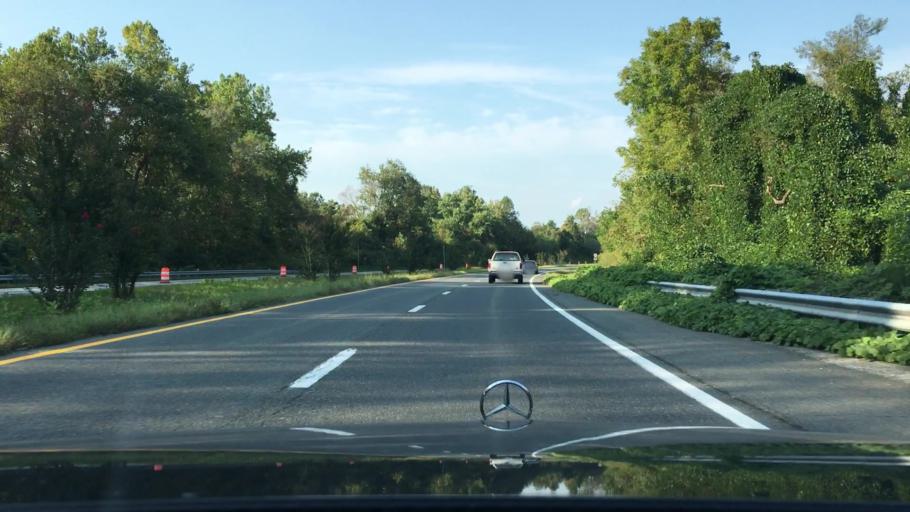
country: US
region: Virginia
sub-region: Amherst County
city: Madison Heights
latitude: 37.5186
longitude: -79.1172
